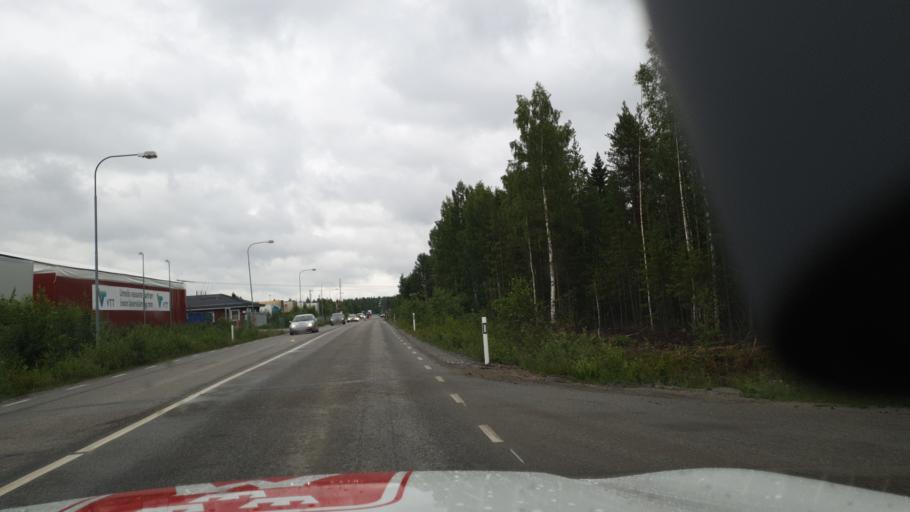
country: SE
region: Vaesterbotten
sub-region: Umea Kommun
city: Roback
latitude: 63.8480
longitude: 20.1413
